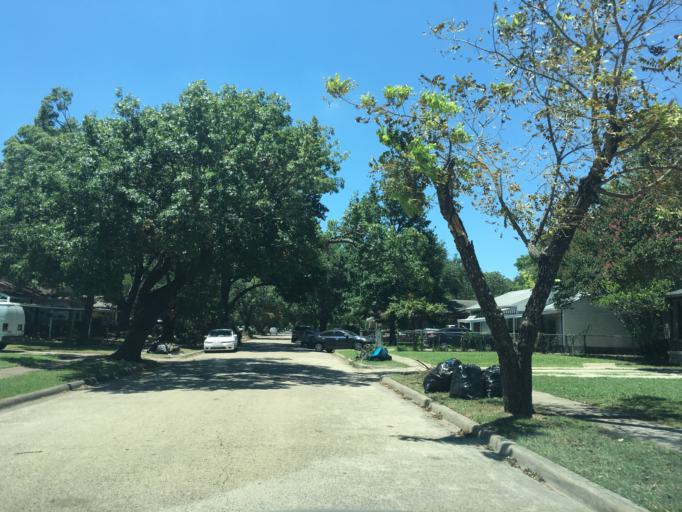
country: US
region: Texas
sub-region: Dallas County
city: Garland
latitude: 32.8487
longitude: -96.6794
